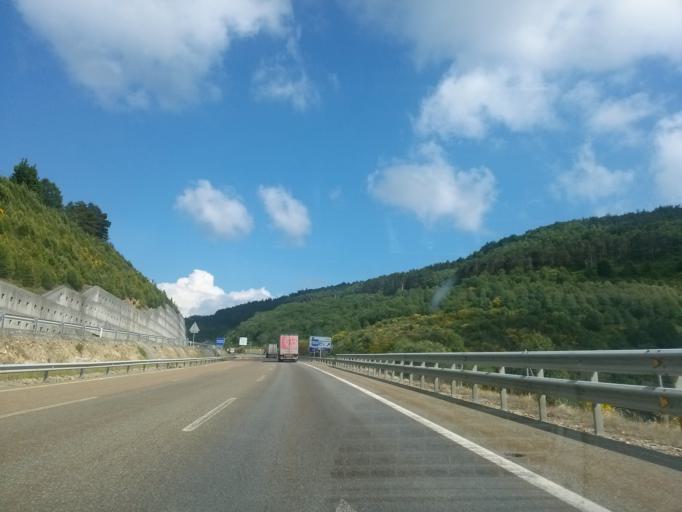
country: ES
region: Castille and Leon
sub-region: Provincia de Leon
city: Balboa
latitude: 42.7287
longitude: -7.0392
